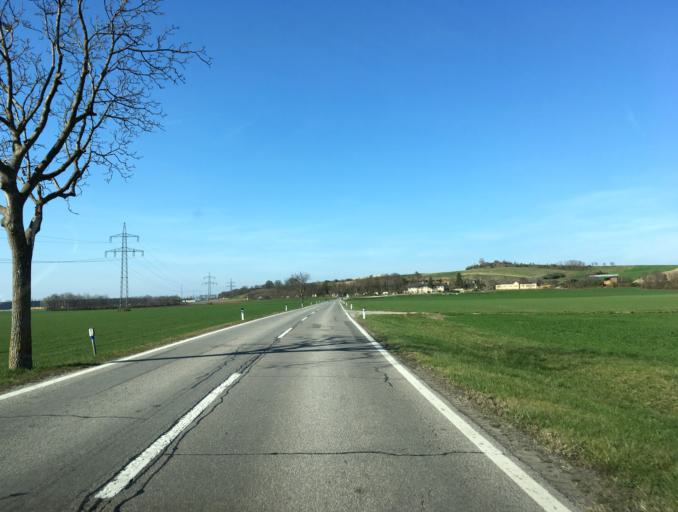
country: AT
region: Lower Austria
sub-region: Politischer Bezirk Bruck an der Leitha
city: Enzersdorf an der Fischa
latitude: 48.0566
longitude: 16.6168
